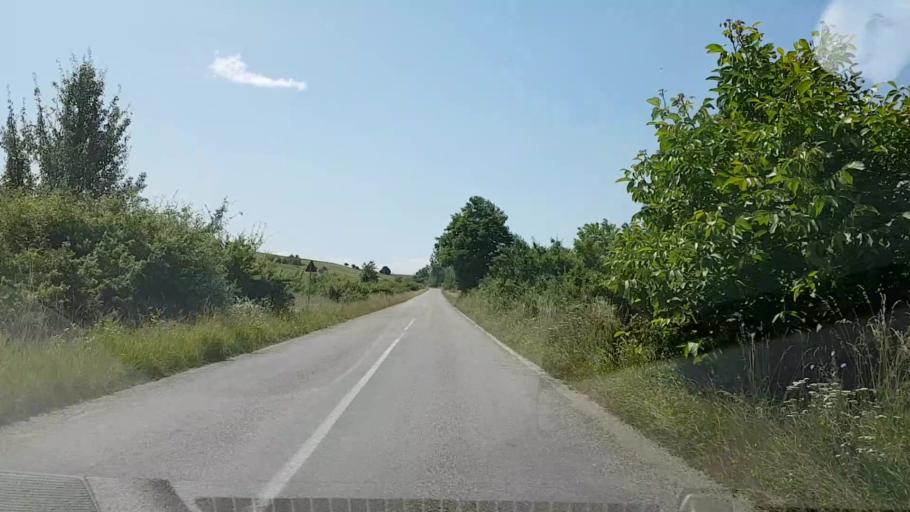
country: RO
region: Brasov
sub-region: Comuna Cincu
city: Cincu
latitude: 45.9487
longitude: 24.7827
